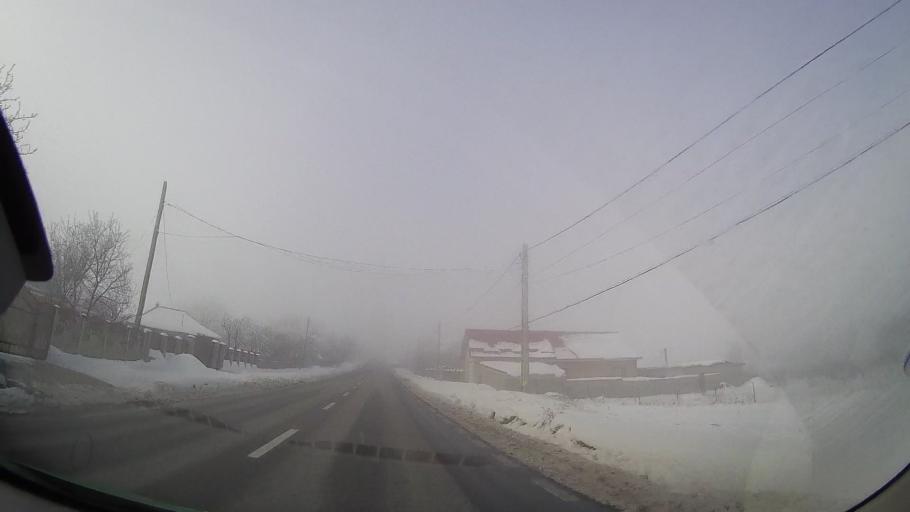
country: RO
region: Iasi
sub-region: Comuna Valea Seaca
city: Topile
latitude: 47.2410
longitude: 26.6672
